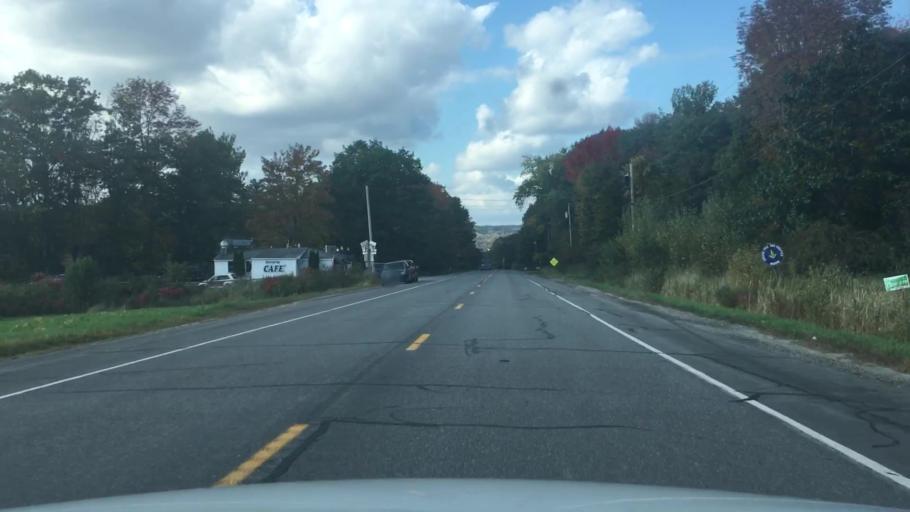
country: US
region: Maine
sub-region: Knox County
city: Union
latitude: 44.2134
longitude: -69.2646
